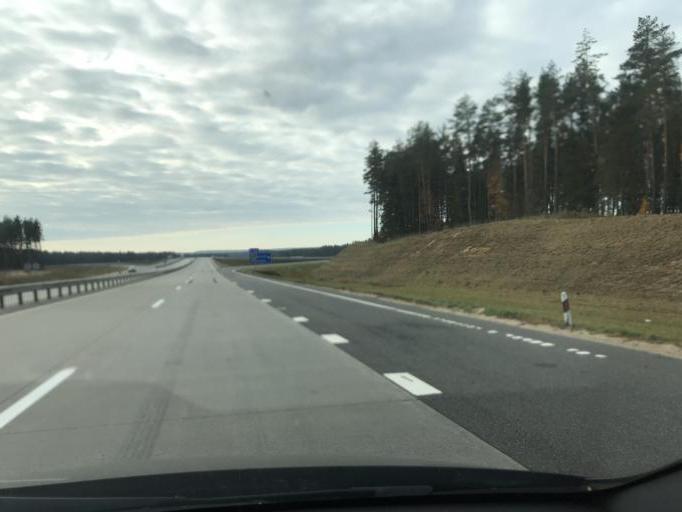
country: BY
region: Minsk
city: Rakaw
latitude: 53.9709
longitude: 27.0922
